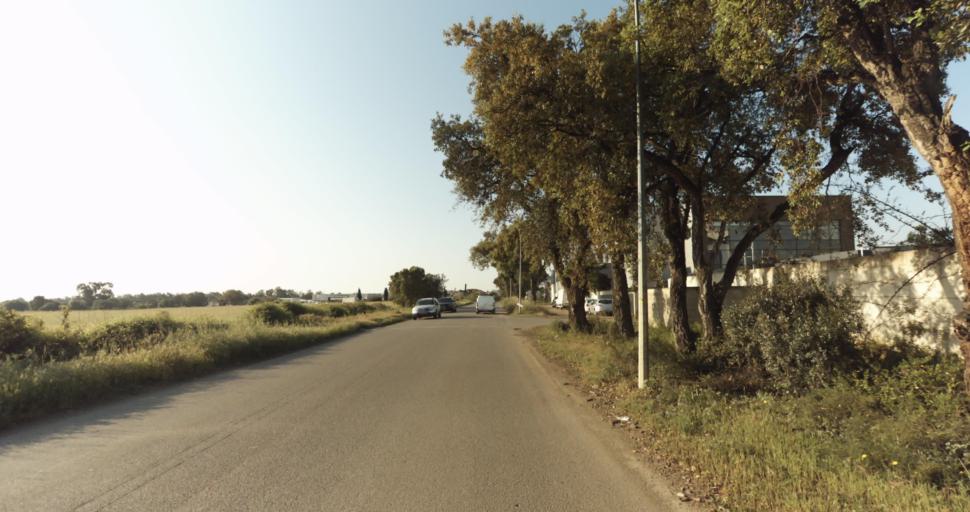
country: FR
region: Corsica
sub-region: Departement de la Haute-Corse
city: Biguglia
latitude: 42.5962
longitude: 9.4420
